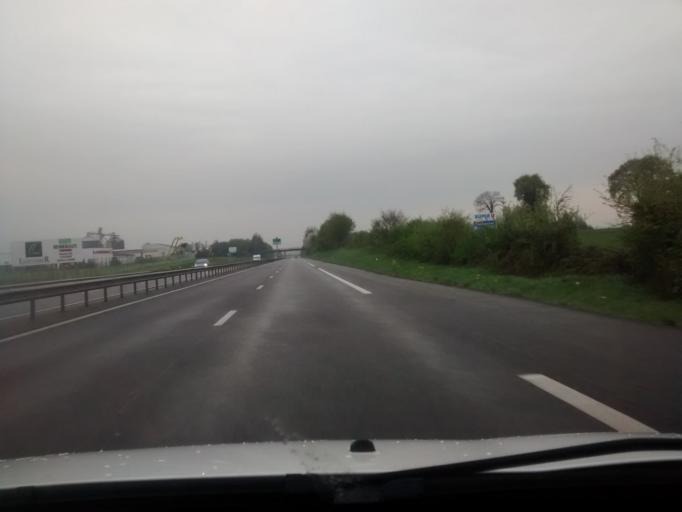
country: FR
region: Brittany
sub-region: Departement des Cotes-d'Armor
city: Broons
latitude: 48.3150
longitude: -2.2446
